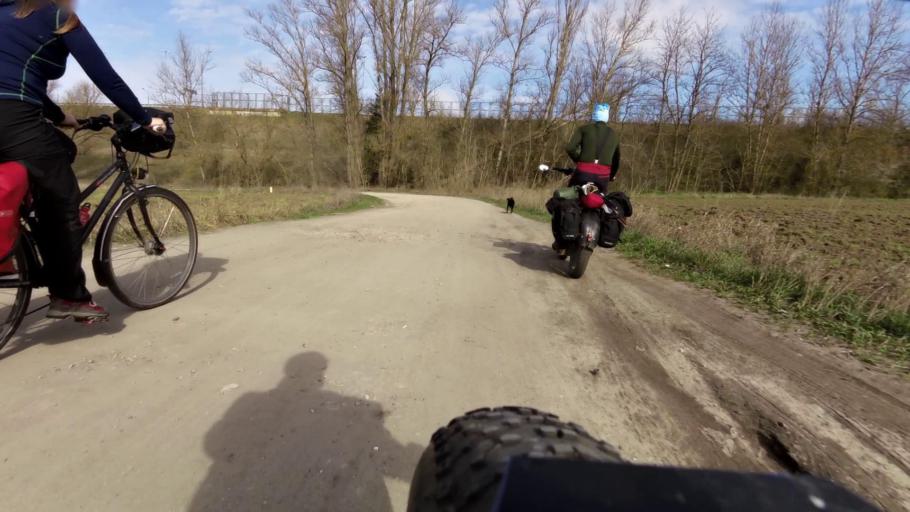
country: PL
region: Lubusz
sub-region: Powiat slubicki
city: Slubice
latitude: 52.3155
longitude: 14.5866
